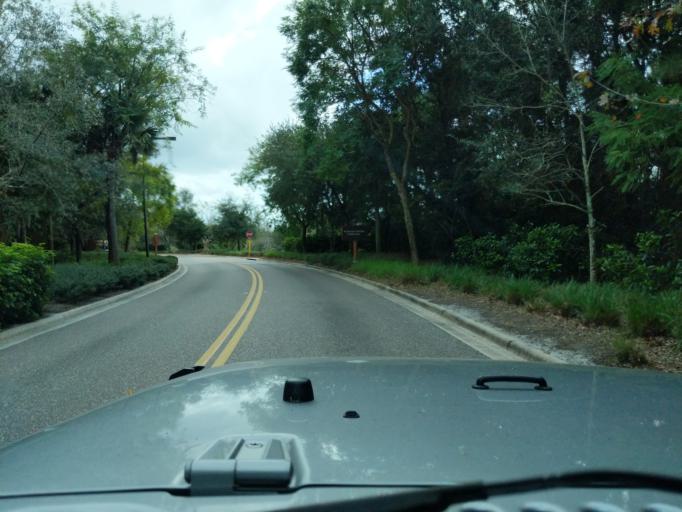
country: US
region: Florida
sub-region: Polk County
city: Citrus Ridge
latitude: 28.3510
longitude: -81.6068
